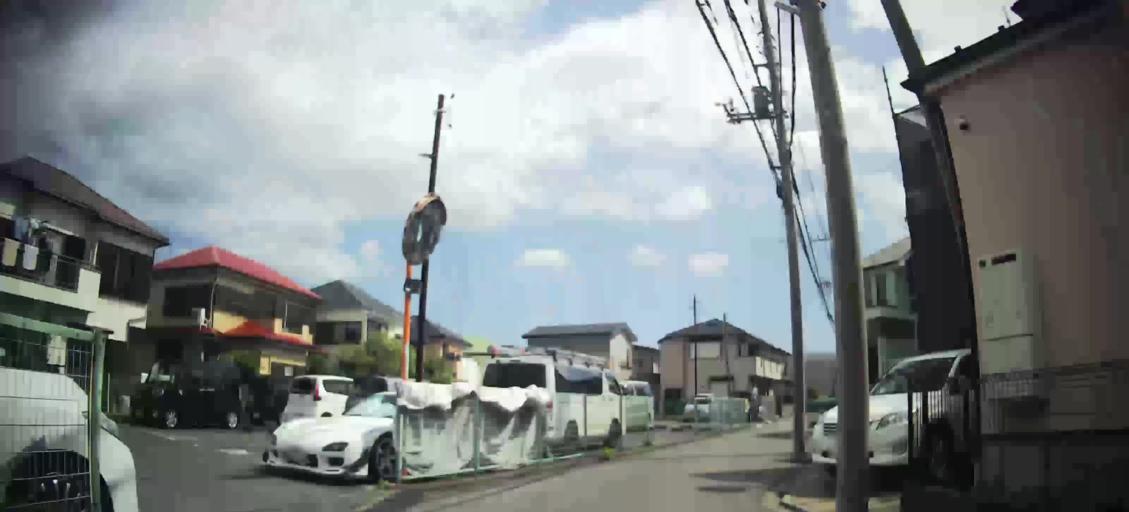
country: JP
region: Kanagawa
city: Minami-rinkan
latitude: 35.4876
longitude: 139.5491
